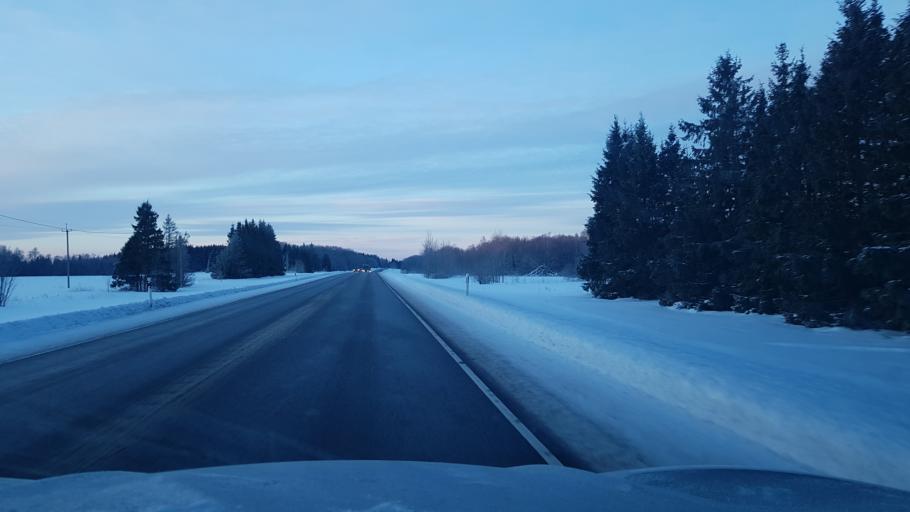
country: EE
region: Ida-Virumaa
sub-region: Narva-Joesuu linn
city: Narva-Joesuu
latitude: 59.3829
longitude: 27.9662
